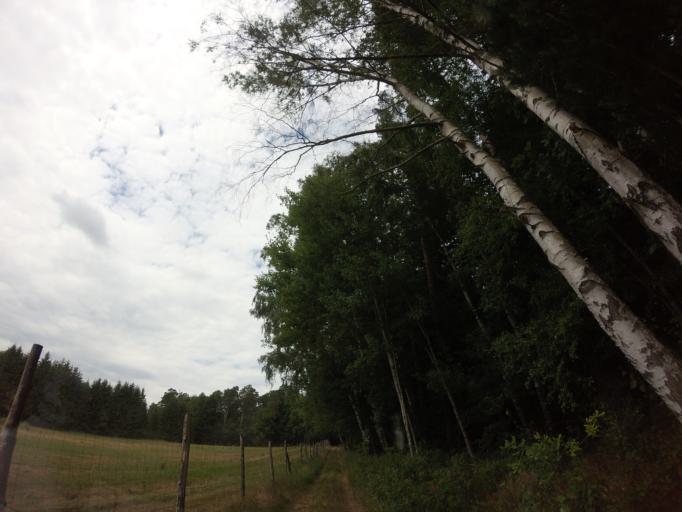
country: PL
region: West Pomeranian Voivodeship
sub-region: Powiat choszczenski
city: Drawno
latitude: 53.1668
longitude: 15.7932
